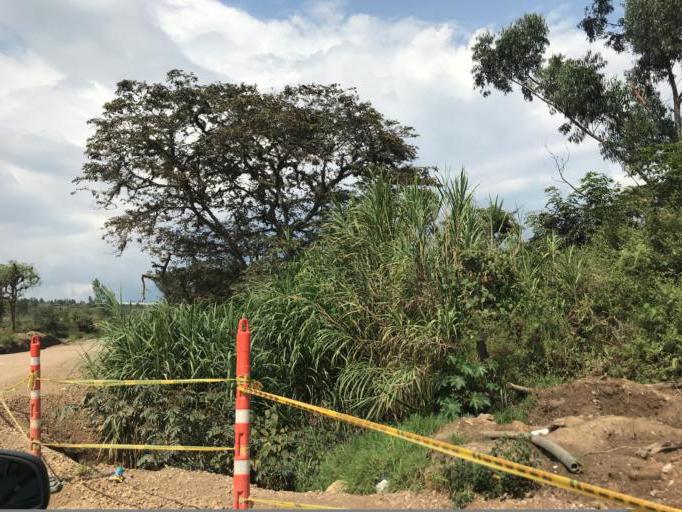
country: CO
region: Boyaca
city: Sutamarchan
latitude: 5.6274
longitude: -73.6126
